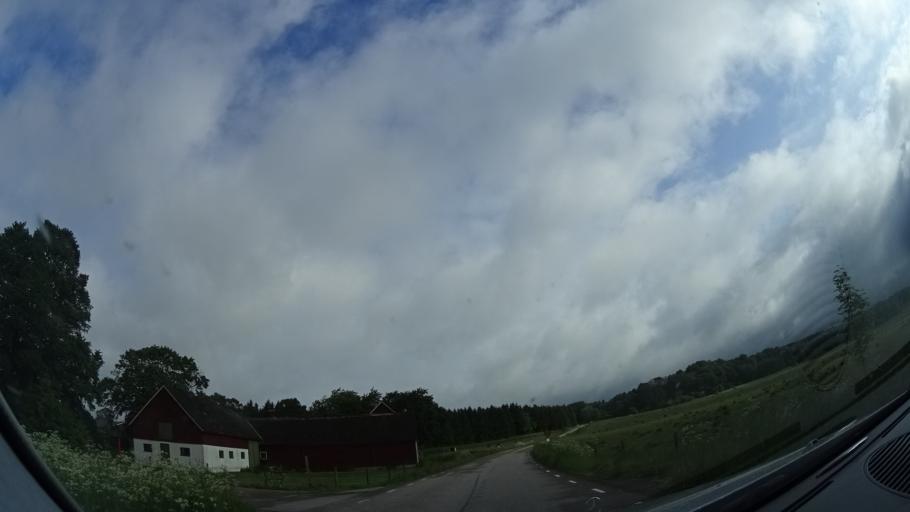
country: SE
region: Skane
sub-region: Eslovs Kommun
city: Stehag
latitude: 55.9485
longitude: 13.4524
